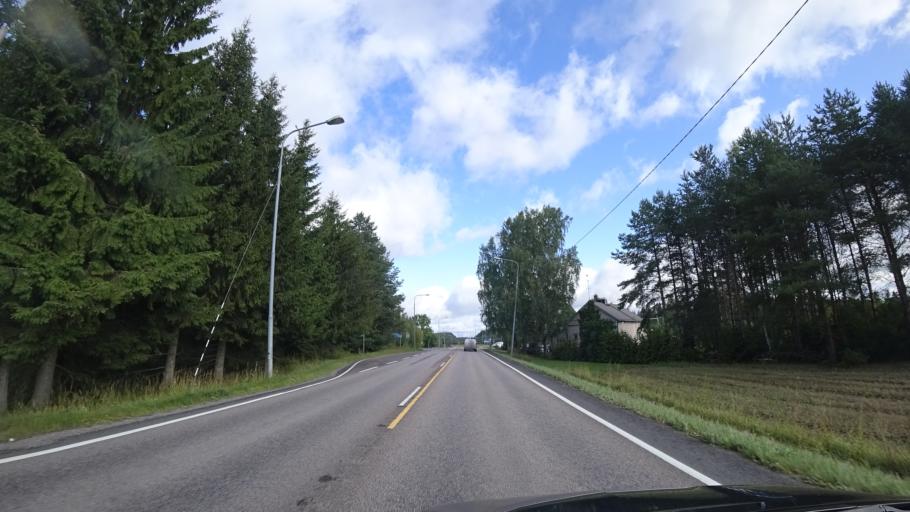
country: FI
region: Uusimaa
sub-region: Helsinki
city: Hyvinge
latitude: 60.5241
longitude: 24.9248
